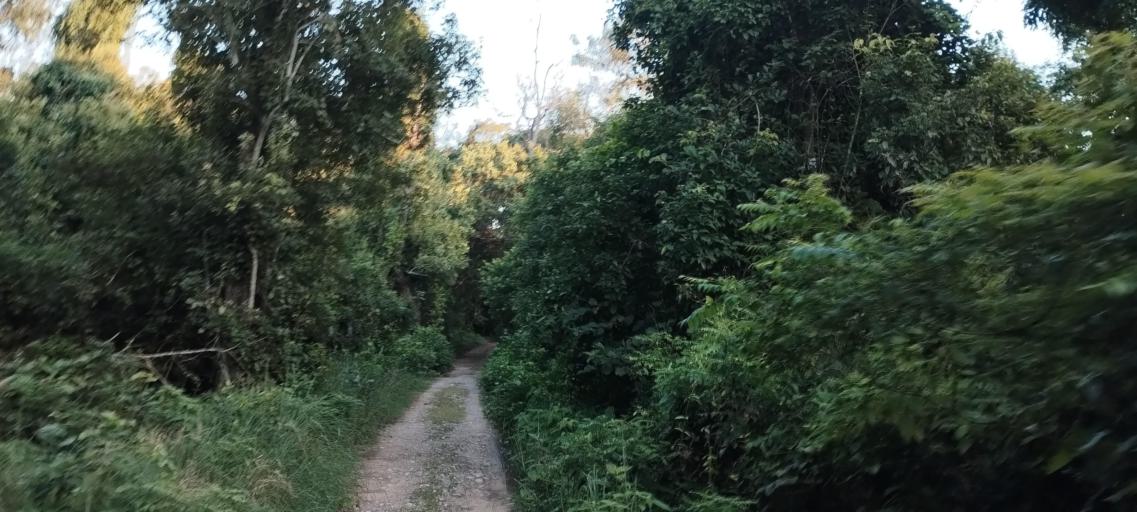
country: NP
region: Far Western
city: Tikapur
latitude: 28.4606
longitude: 81.2412
